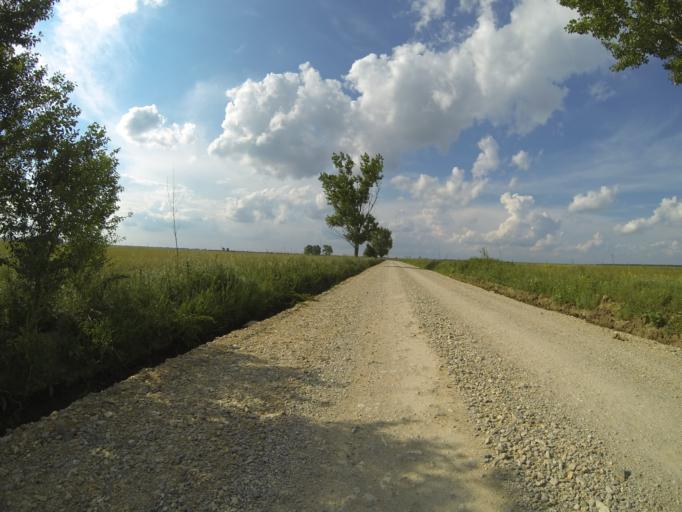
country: RO
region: Dolj
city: Satu Nou Calopar
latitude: 44.1424
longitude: 23.7942
